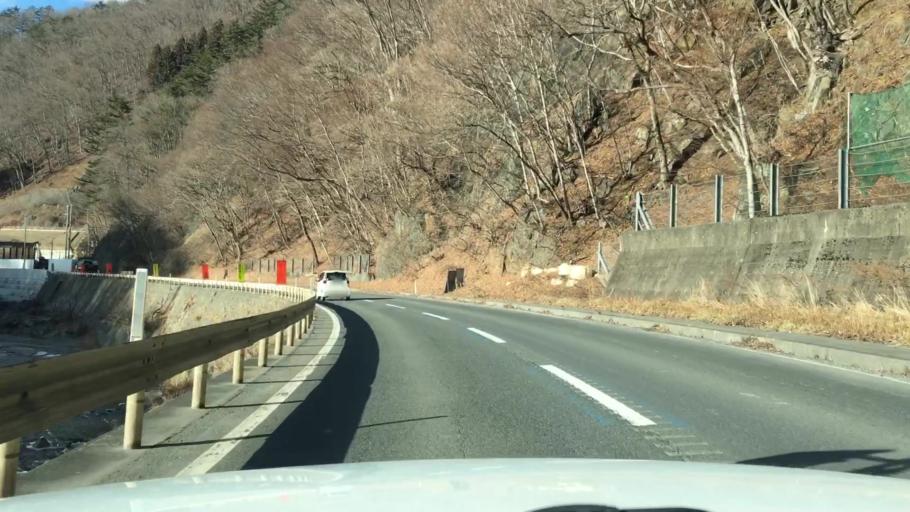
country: JP
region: Iwate
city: Miyako
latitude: 39.6002
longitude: 141.7128
